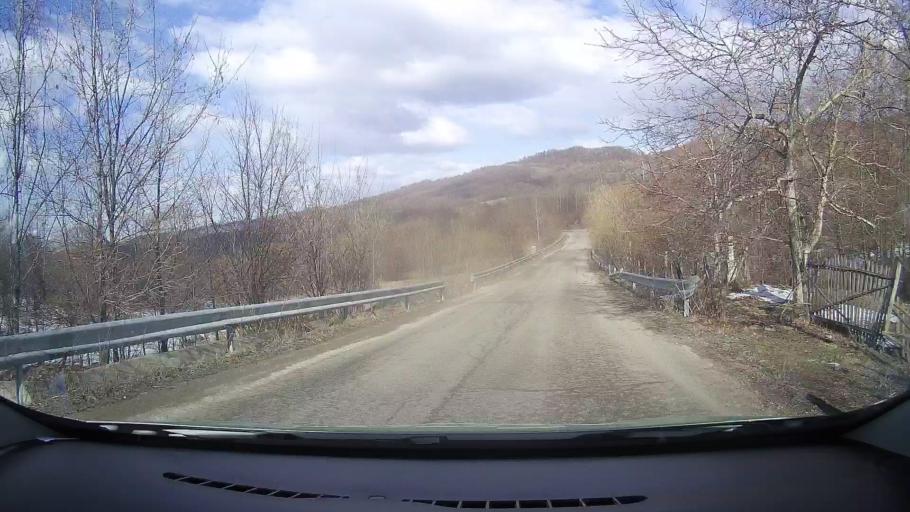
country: RO
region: Dambovita
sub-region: Oras Pucioasa
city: Glodeni
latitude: 45.0909
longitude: 25.4686
